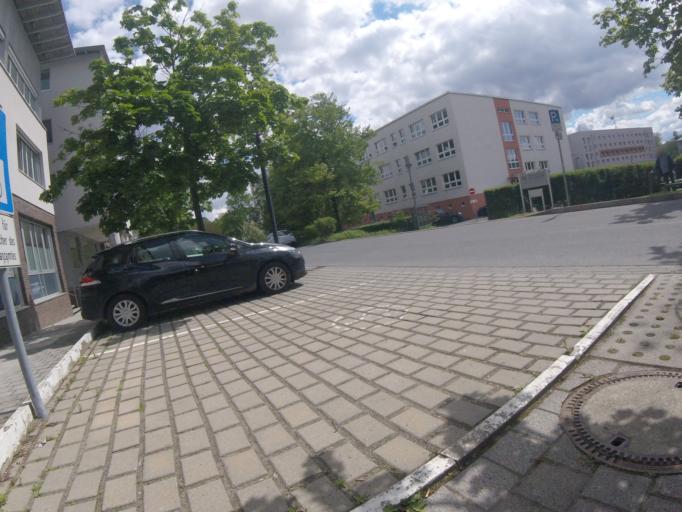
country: DE
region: Brandenburg
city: Konigs Wusterhausen
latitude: 52.3008
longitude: 13.6282
